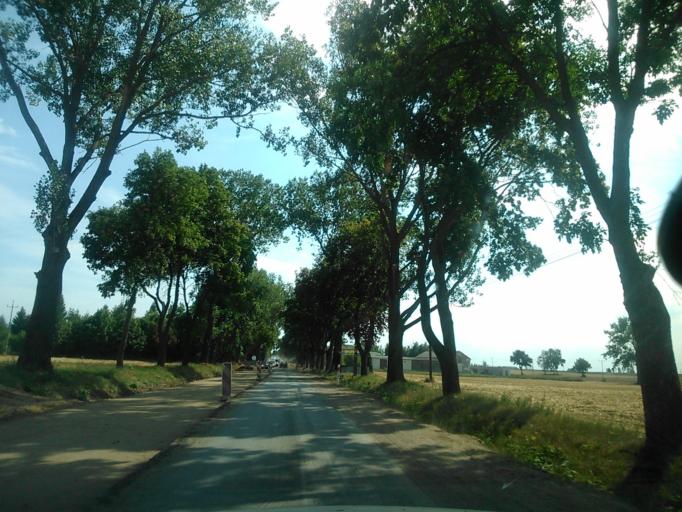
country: PL
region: Warmian-Masurian Voivodeship
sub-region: Powiat dzialdowski
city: Dzialdowo
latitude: 53.2283
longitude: 20.1938
